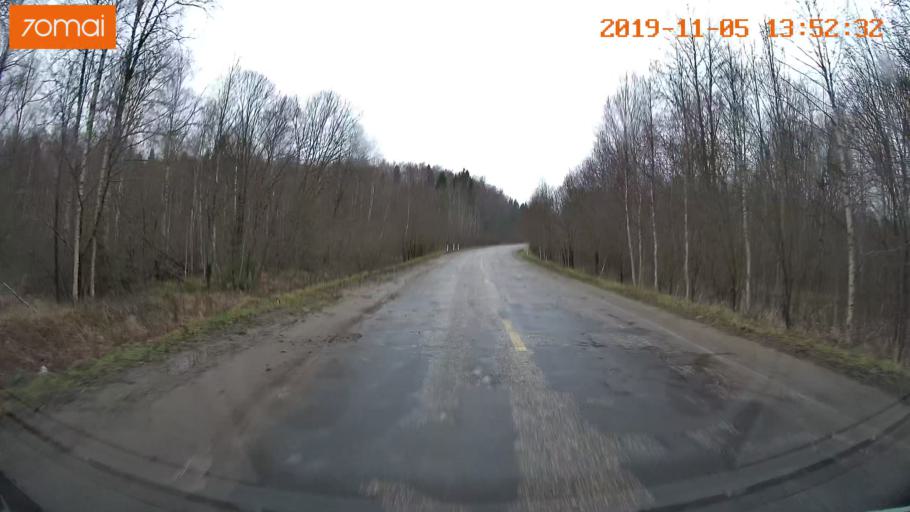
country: RU
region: Ivanovo
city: Kaminskiy
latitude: 57.0279
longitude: 41.3845
